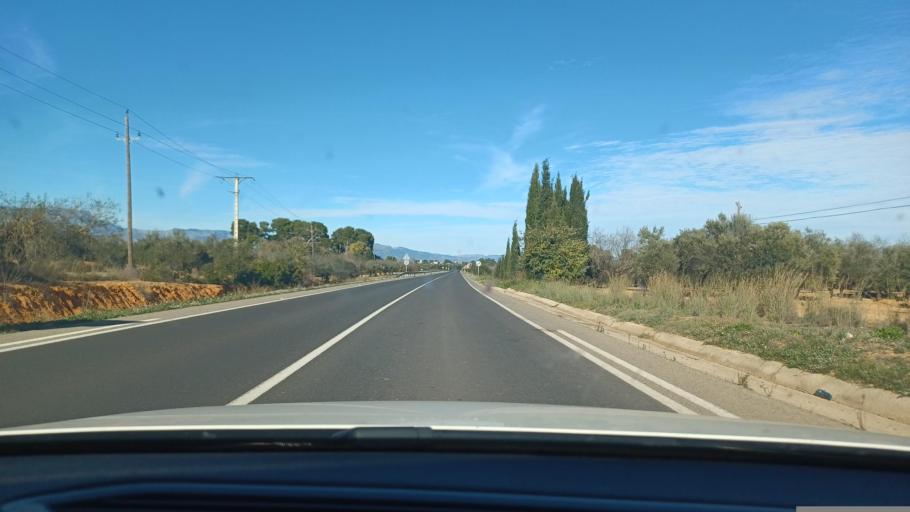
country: ES
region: Catalonia
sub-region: Provincia de Tarragona
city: Santa Barbara
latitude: 40.6909
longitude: 0.5066
